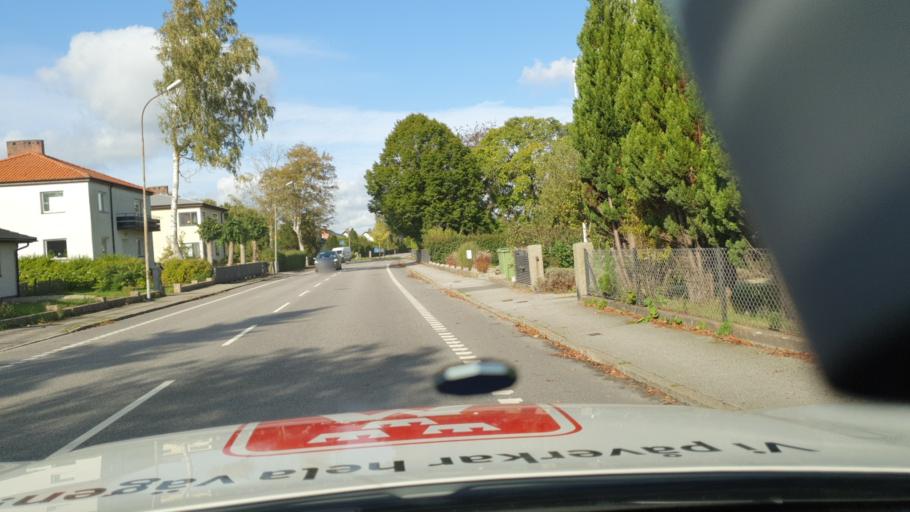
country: SE
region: Skane
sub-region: Tomelilla Kommun
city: Tomelilla
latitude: 55.5360
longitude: 13.9575
